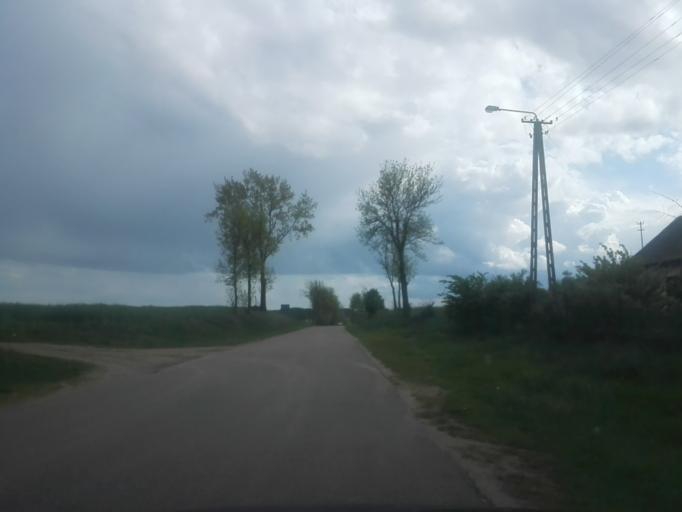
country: PL
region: Podlasie
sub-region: Powiat lomzynski
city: Wizna
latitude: 53.2758
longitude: 22.4539
